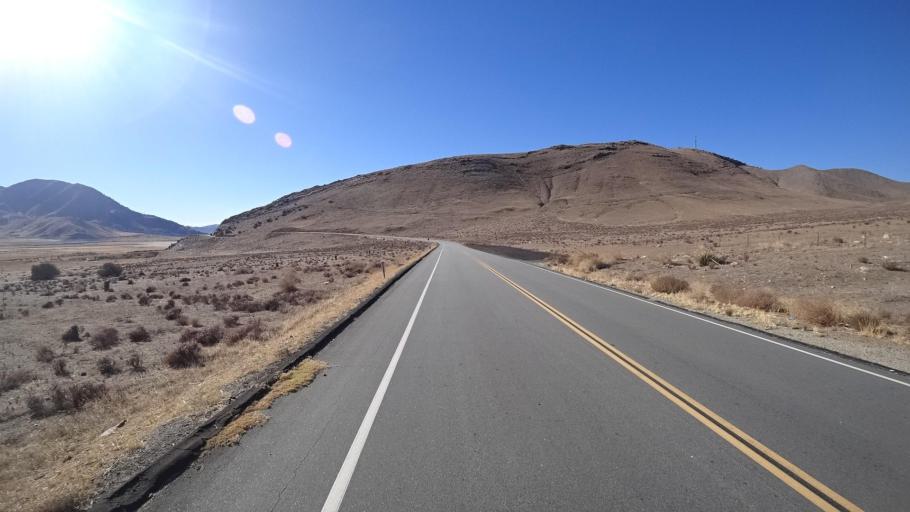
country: US
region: California
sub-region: Kern County
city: Wofford Heights
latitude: 35.6806
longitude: -118.4092
